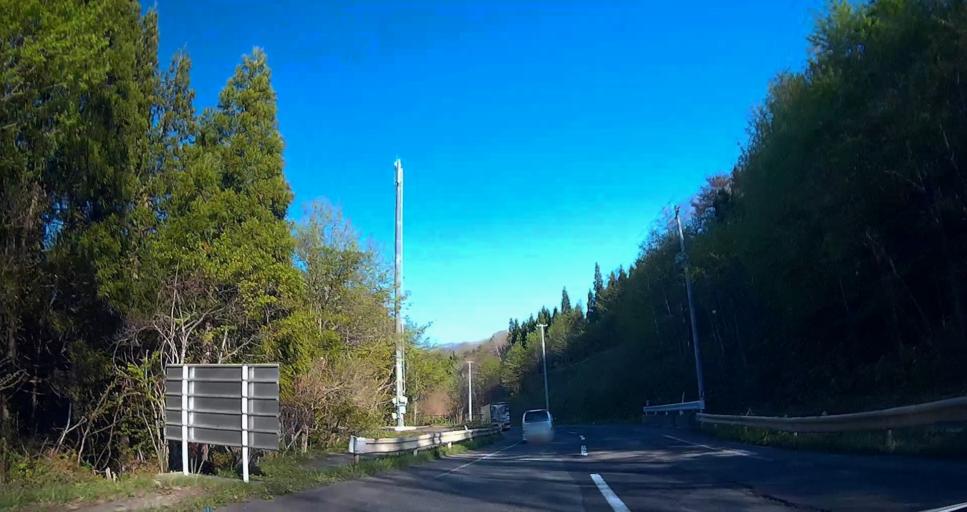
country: JP
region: Aomori
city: Mutsu
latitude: 41.4306
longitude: 141.1386
